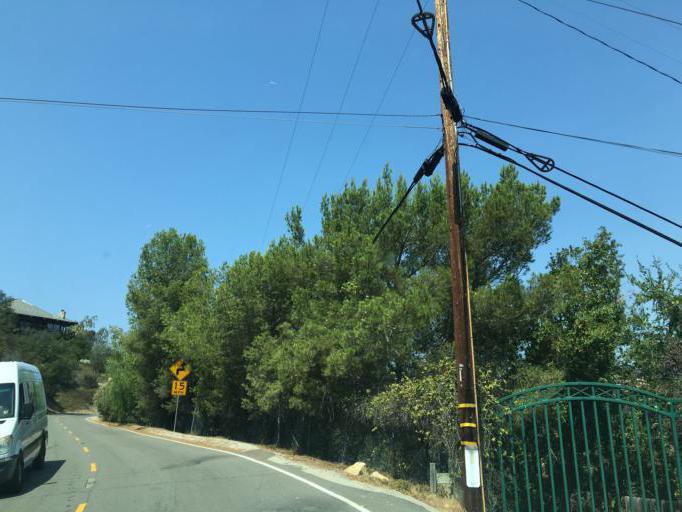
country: US
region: California
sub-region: Los Angeles County
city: Topanga
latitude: 34.0699
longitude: -118.6053
